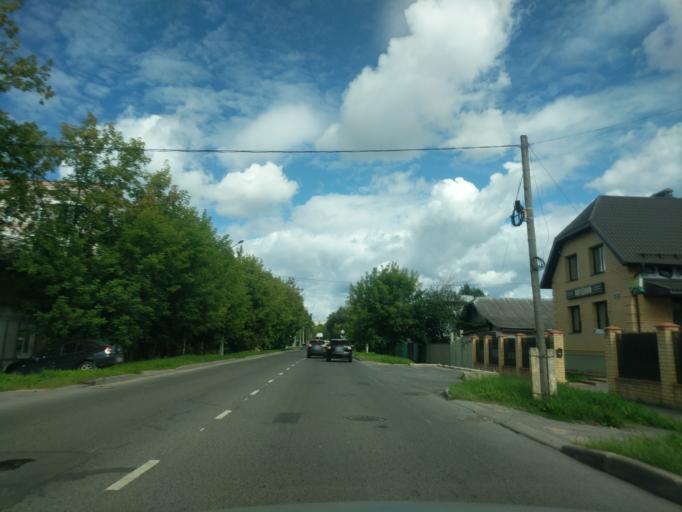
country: RU
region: Kostroma
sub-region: Kostromskoy Rayon
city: Kostroma
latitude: 57.7771
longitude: 40.9542
